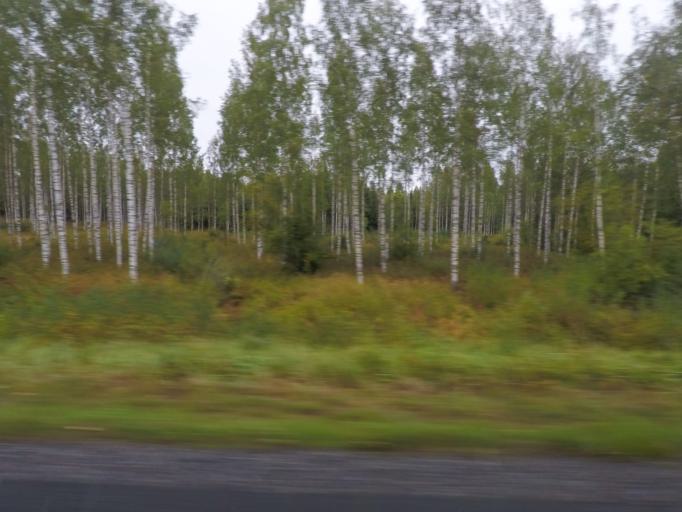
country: FI
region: Northern Savo
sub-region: Varkaus
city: Leppaevirta
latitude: 62.5176
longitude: 27.6890
